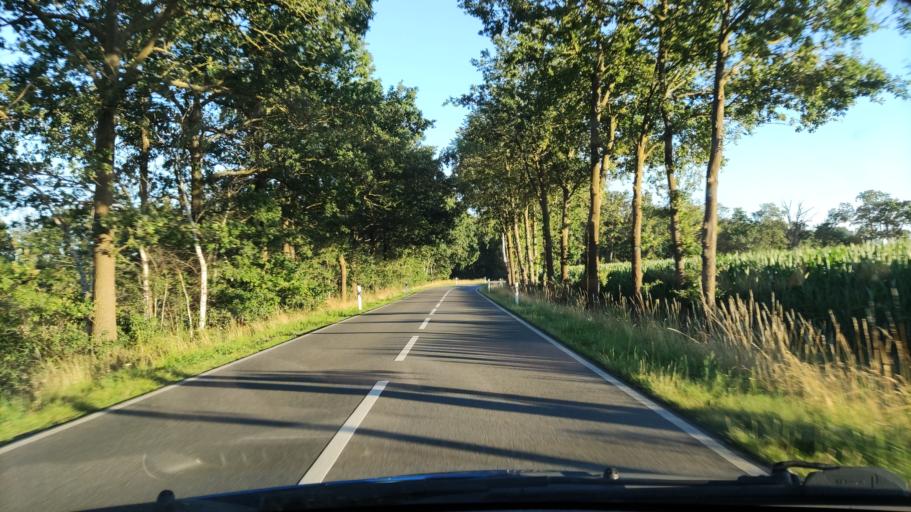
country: DE
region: Lower Saxony
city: Jameln
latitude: 53.0341
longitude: 11.1295
